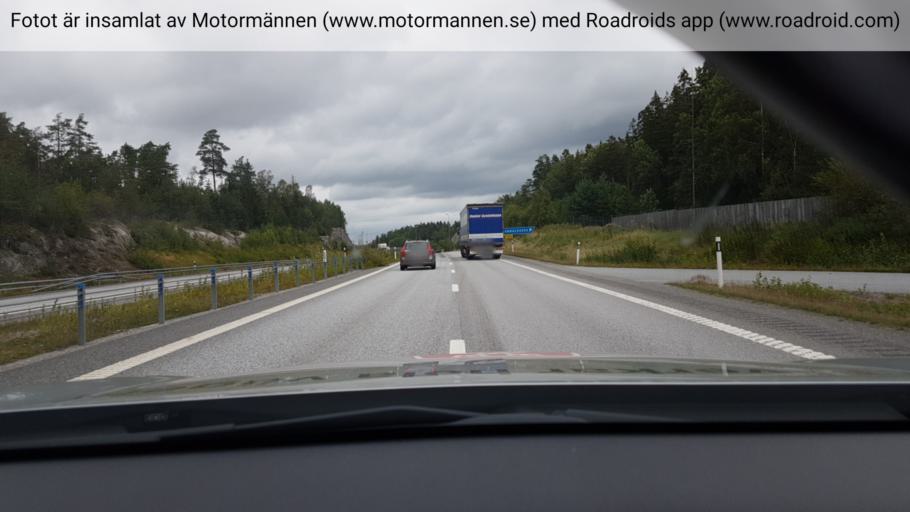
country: SE
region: Vaestra Goetaland
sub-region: Tanums Kommun
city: Tanumshede
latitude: 58.6124
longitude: 11.4551
